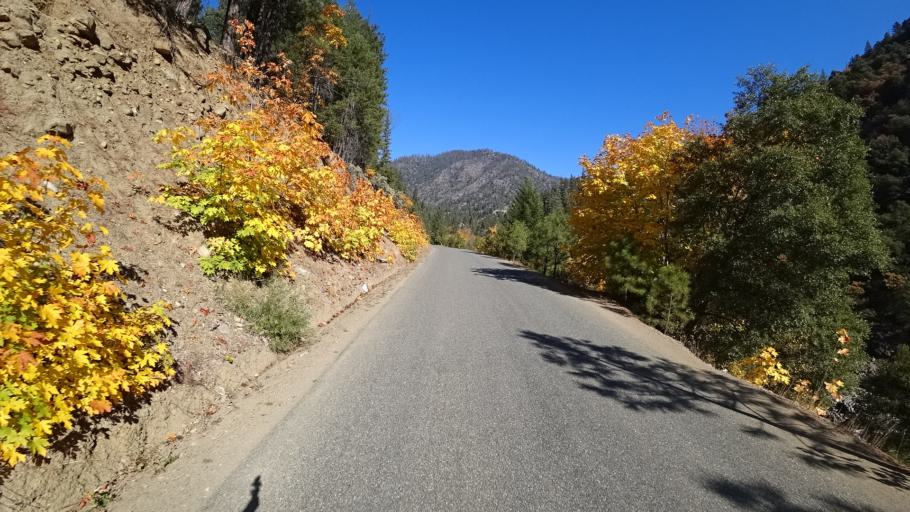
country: US
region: California
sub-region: Siskiyou County
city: Happy Camp
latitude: 41.6746
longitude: -123.1025
